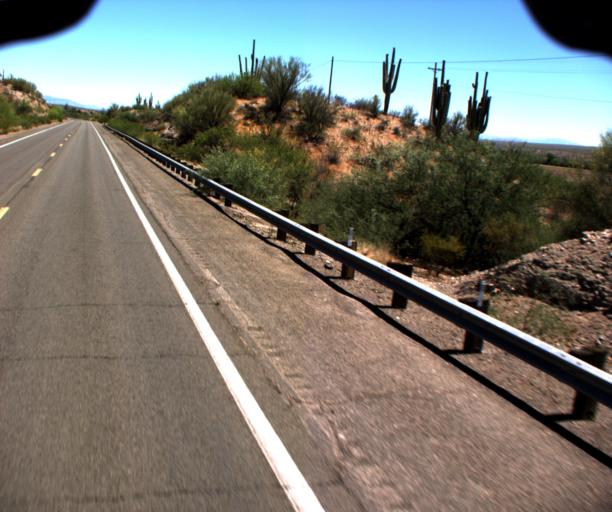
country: US
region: Arizona
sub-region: Pinal County
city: Kearny
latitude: 32.9718
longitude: -110.7626
